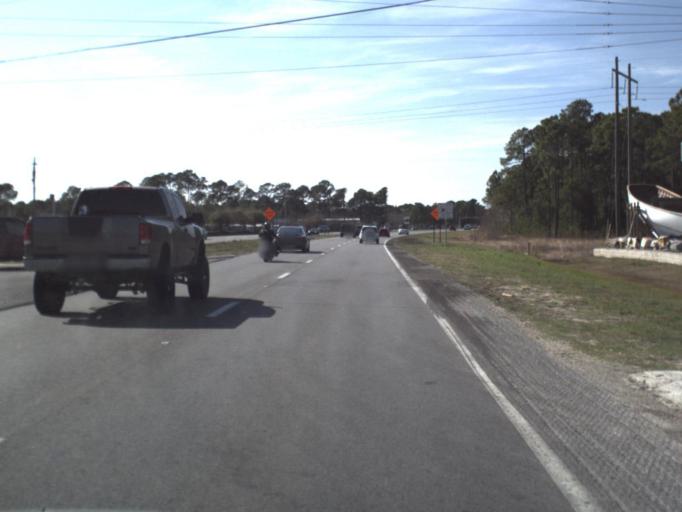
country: US
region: Florida
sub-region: Bay County
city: Panama City Beach
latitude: 30.1896
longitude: -85.7865
